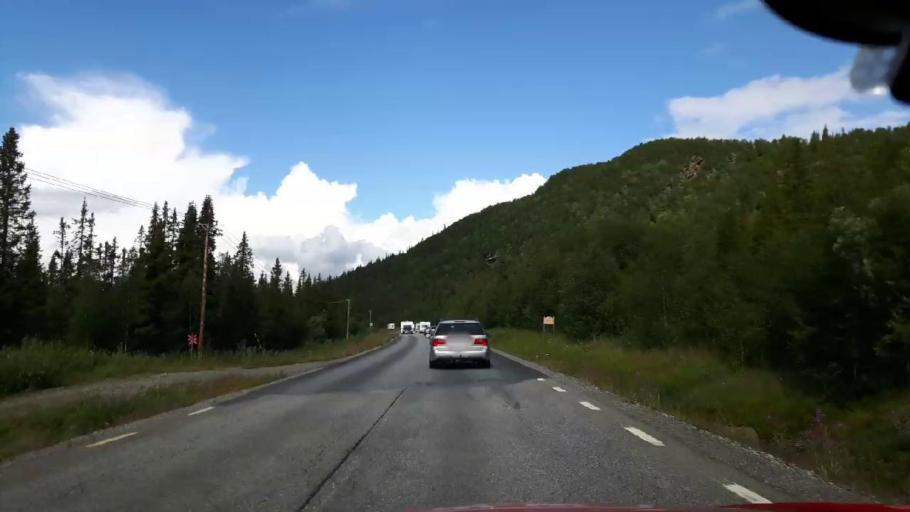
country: SE
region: Vaesterbotten
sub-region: Vilhelmina Kommun
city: Sjoberg
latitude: 65.0355
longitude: 15.1359
